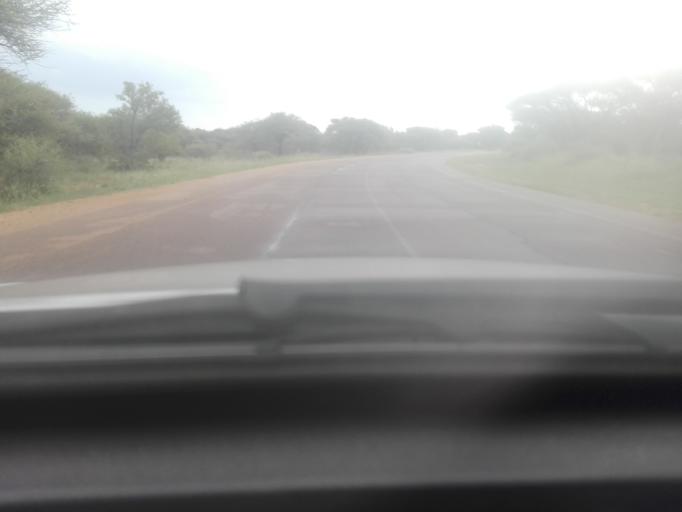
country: BW
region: Kweneng
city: Mmopone
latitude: -24.5595
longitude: 25.9281
